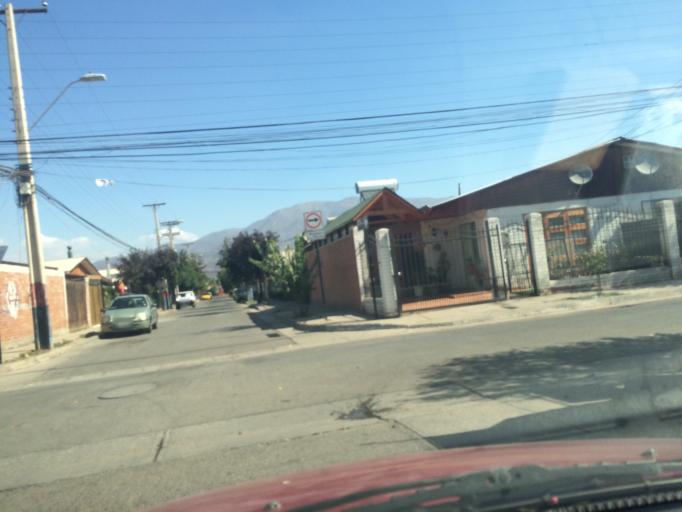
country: CL
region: Valparaiso
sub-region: Provincia de Los Andes
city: Los Andes
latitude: -32.8481
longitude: -70.5942
